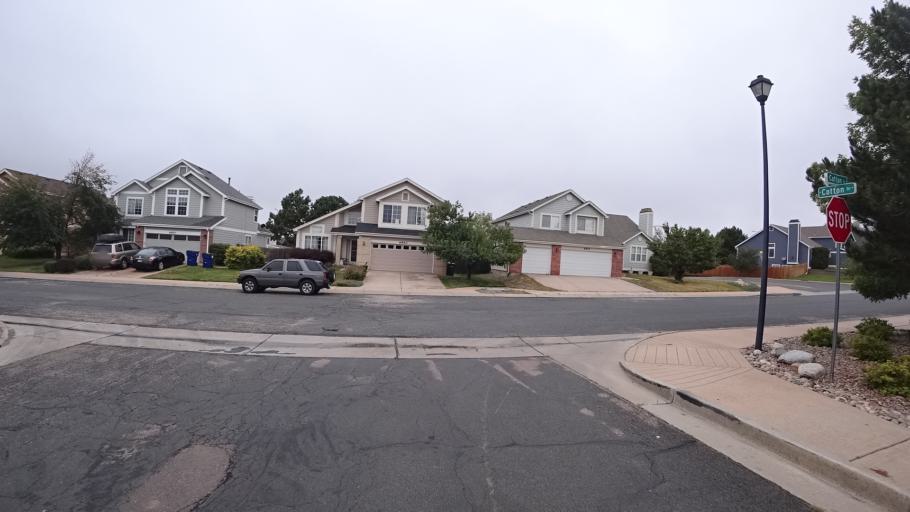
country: US
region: Colorado
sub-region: El Paso County
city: Cimarron Hills
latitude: 38.9324
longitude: -104.7531
